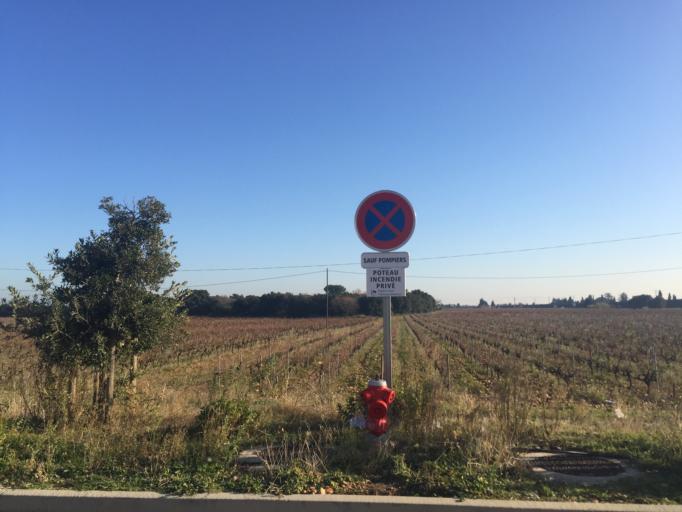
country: FR
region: Provence-Alpes-Cote d'Azur
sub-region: Departement du Vaucluse
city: Courthezon
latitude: 44.1094
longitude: 4.8536
